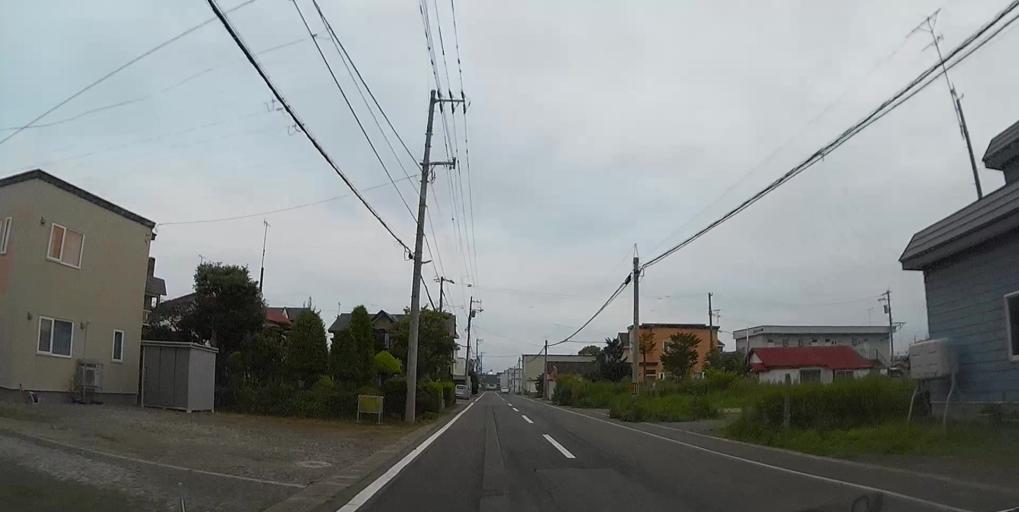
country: JP
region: Hokkaido
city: Nanae
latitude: 42.2545
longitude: 140.2622
